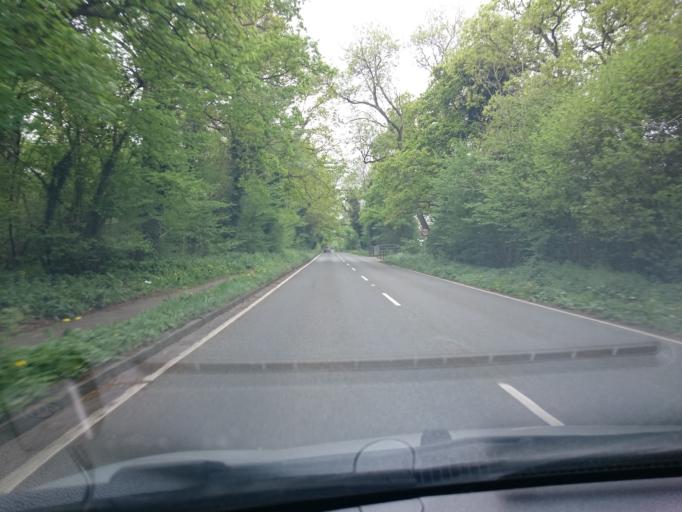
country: GB
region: England
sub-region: Surrey
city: Normandy
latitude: 51.2613
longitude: -0.6514
